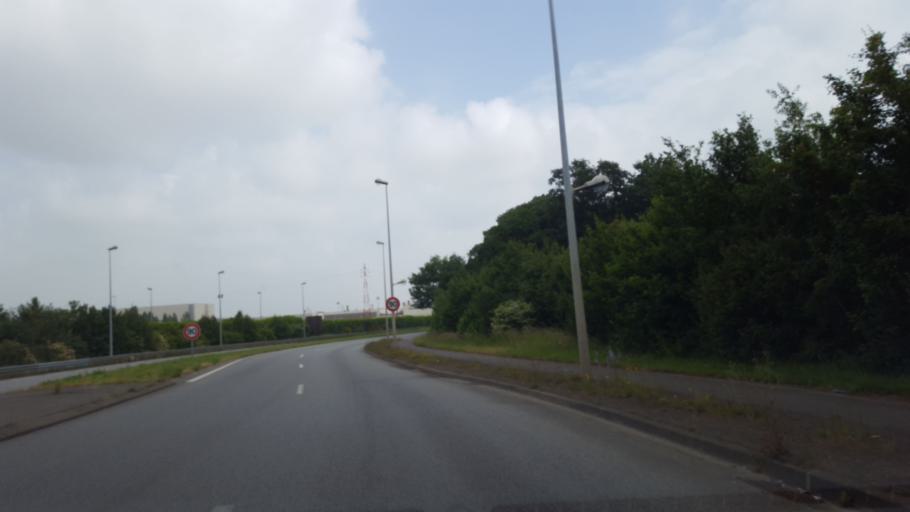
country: FR
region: Brittany
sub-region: Departement d'Ille-et-Vilaine
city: Chartres-de-Bretagne
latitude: 48.0502
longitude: -1.7067
